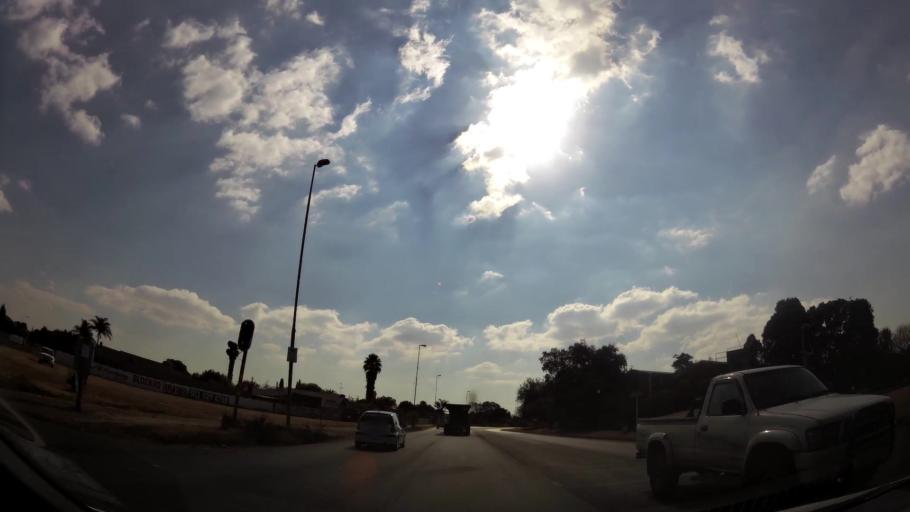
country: ZA
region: Gauteng
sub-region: Ekurhuleni Metropolitan Municipality
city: Boksburg
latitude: -26.1875
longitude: 28.2170
